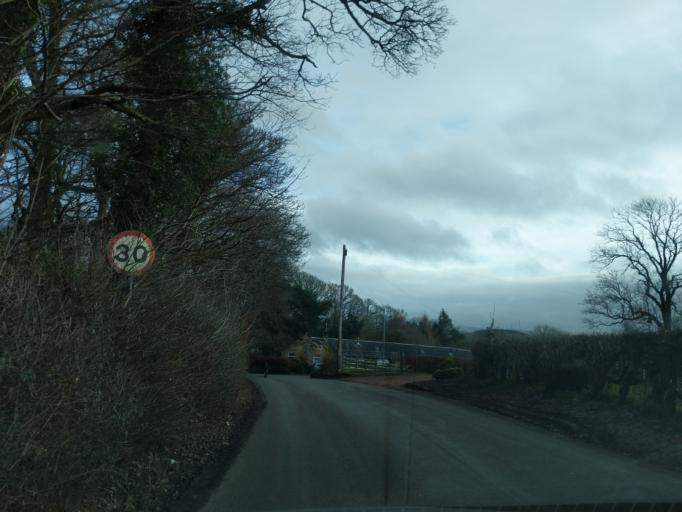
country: GB
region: Scotland
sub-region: South Lanarkshire
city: Carluke
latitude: 55.7096
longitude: -3.8466
